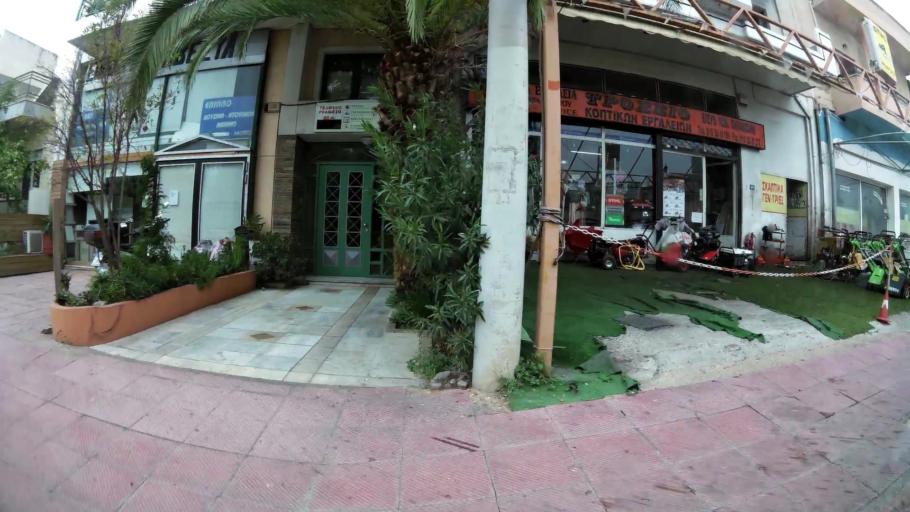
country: GR
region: Attica
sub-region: Nomarchia Athinas
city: Agioi Anargyroi
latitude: 38.0332
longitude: 23.7167
